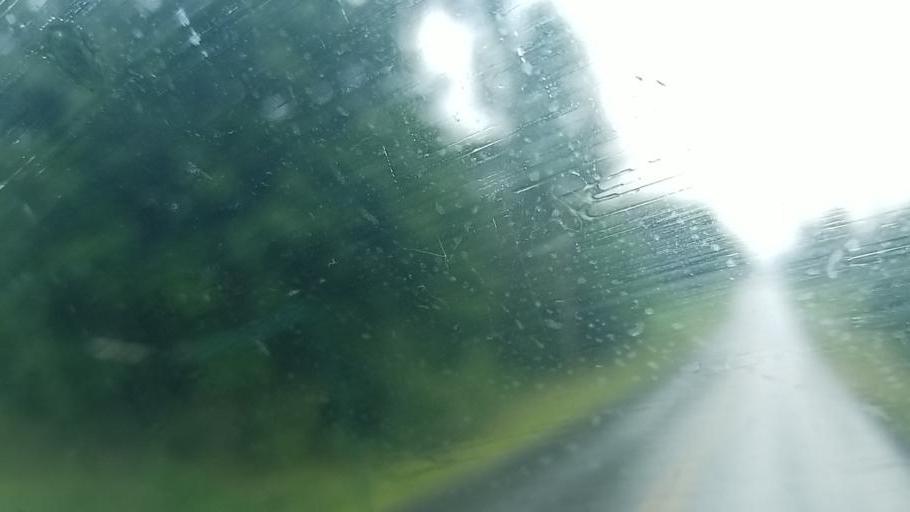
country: US
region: Ohio
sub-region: Lorain County
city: Grafton
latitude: 41.1850
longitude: -82.0448
